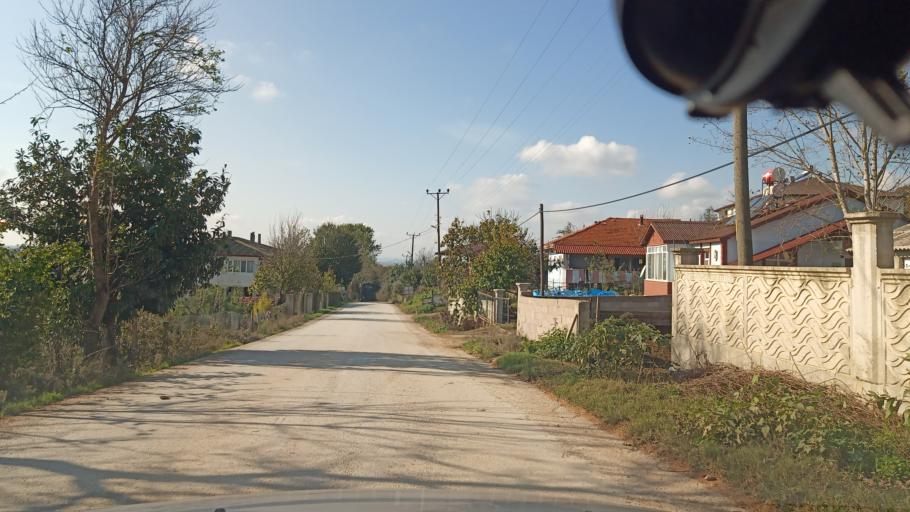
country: TR
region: Sakarya
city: Ferizli
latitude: 41.0964
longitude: 30.4643
